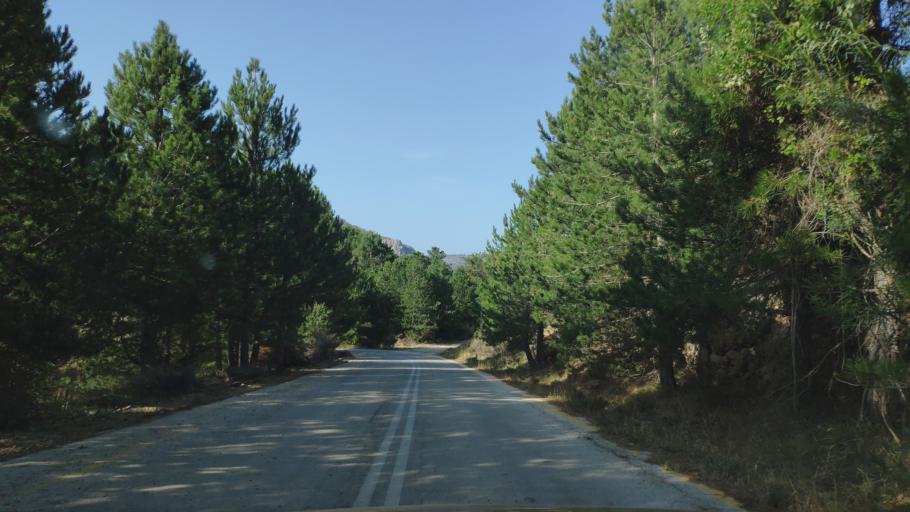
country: GR
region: West Greece
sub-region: Nomos Achaias
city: Aiyira
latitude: 38.0560
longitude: 22.3818
